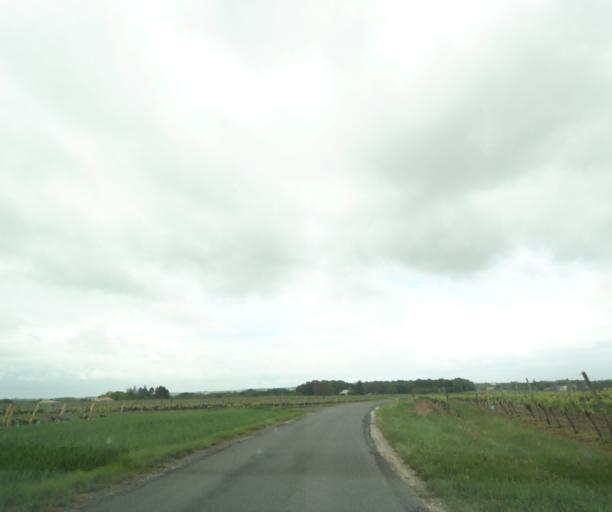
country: FR
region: Poitou-Charentes
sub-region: Departement de la Charente-Maritime
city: Perignac
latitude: 45.6759
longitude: -0.4961
